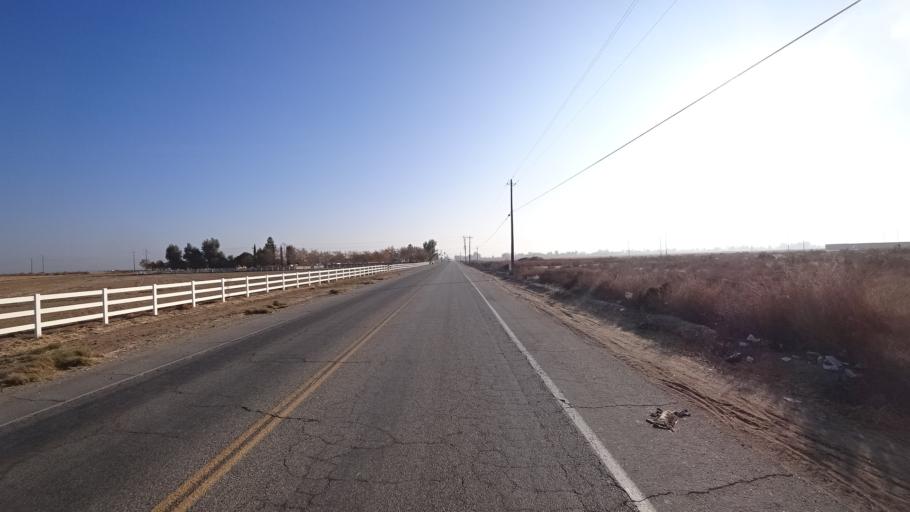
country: US
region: California
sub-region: Kern County
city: Greenfield
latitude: 35.2524
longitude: -118.9789
